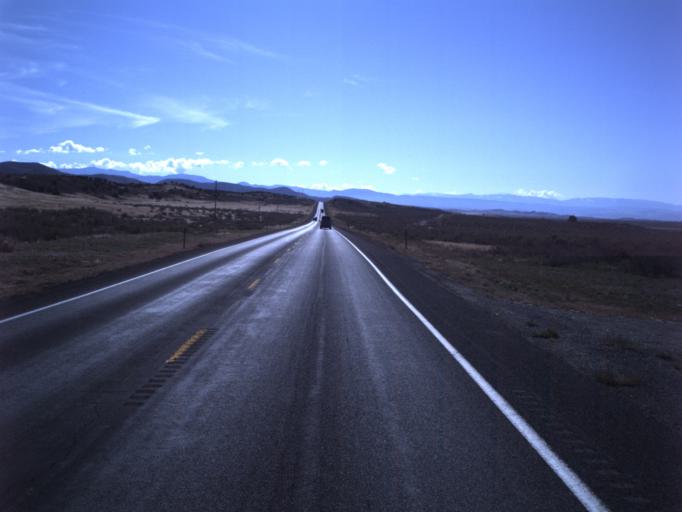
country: US
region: Utah
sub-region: Sanpete County
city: Gunnison
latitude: 39.2964
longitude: -111.8907
